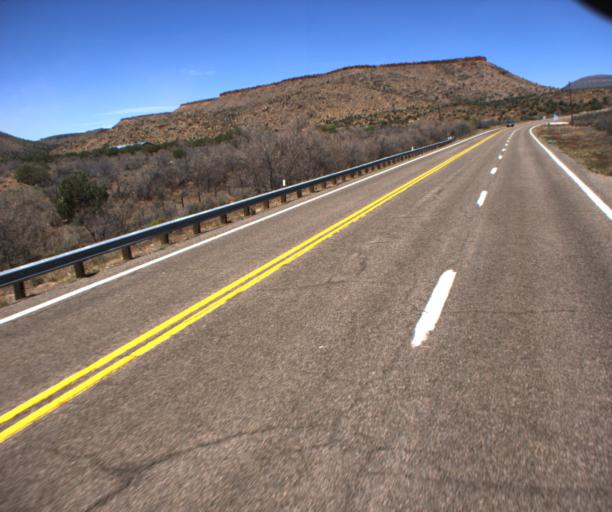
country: US
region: Arizona
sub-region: Mohave County
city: Peach Springs
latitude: 35.4227
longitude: -113.6488
